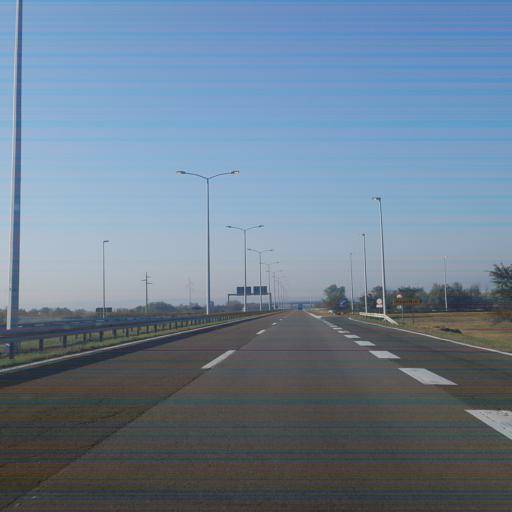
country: RS
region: Central Serbia
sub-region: Nisavski Okrug
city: Nis
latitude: 43.3280
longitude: 21.8109
